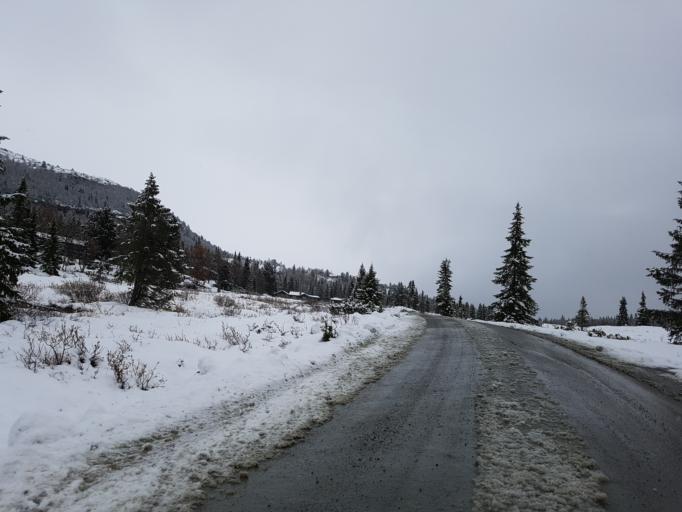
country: NO
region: Oppland
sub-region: Sel
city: Otta
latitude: 61.8053
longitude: 9.6919
